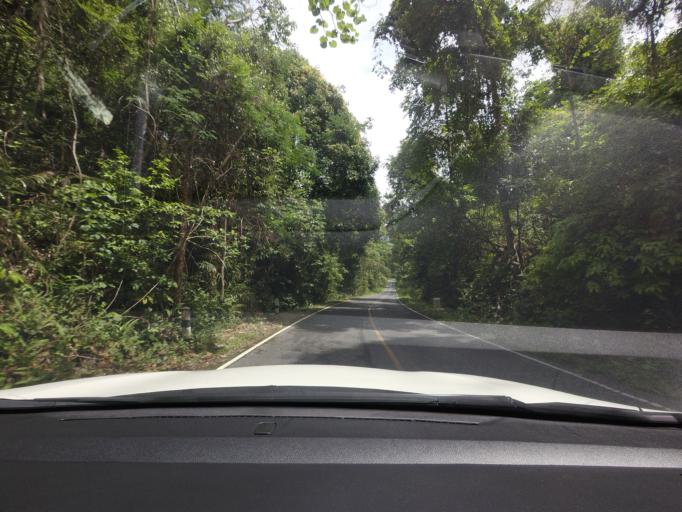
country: TH
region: Nakhon Nayok
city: Pak Phli
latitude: 14.2809
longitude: 101.3929
